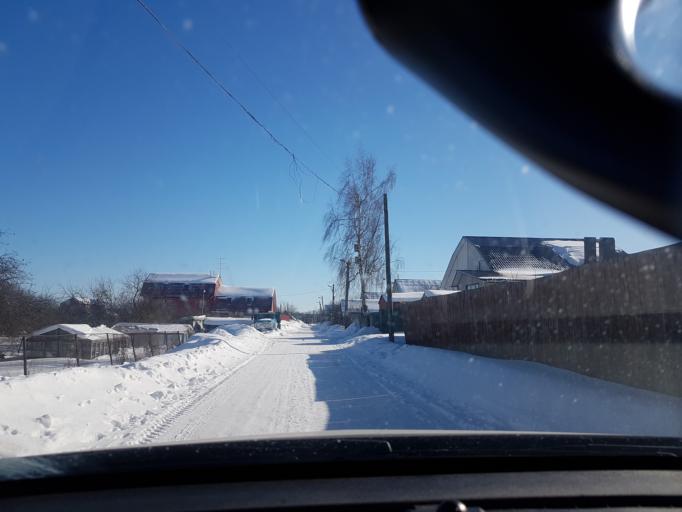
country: RU
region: Moskovskaya
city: Sychevo
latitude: 56.0138
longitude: 36.2274
